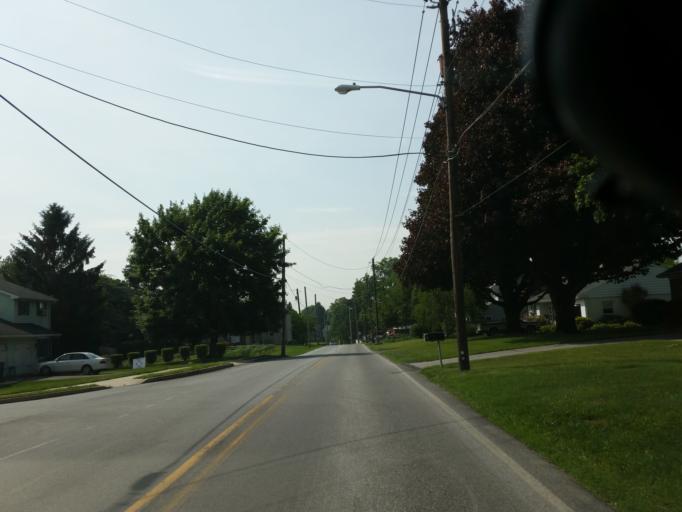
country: US
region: Pennsylvania
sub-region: Lancaster County
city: Strasburg
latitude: 39.9871
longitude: -76.1914
